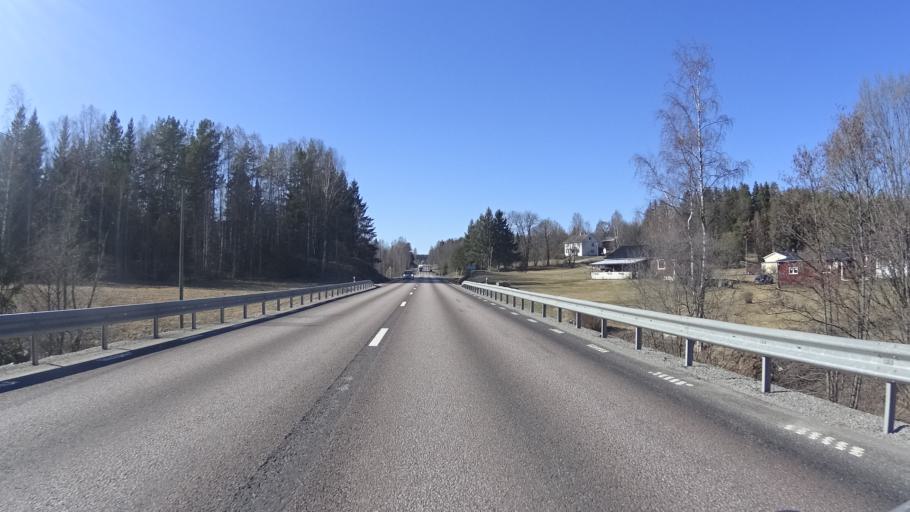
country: SE
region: Vaermland
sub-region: Sunne Kommun
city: Sunne
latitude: 59.6618
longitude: 12.9260
